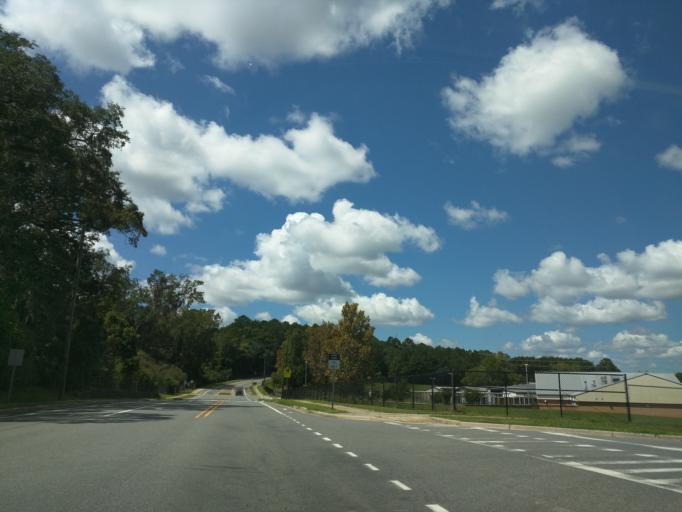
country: US
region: Florida
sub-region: Leon County
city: Tallahassee
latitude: 30.4347
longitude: -84.2144
